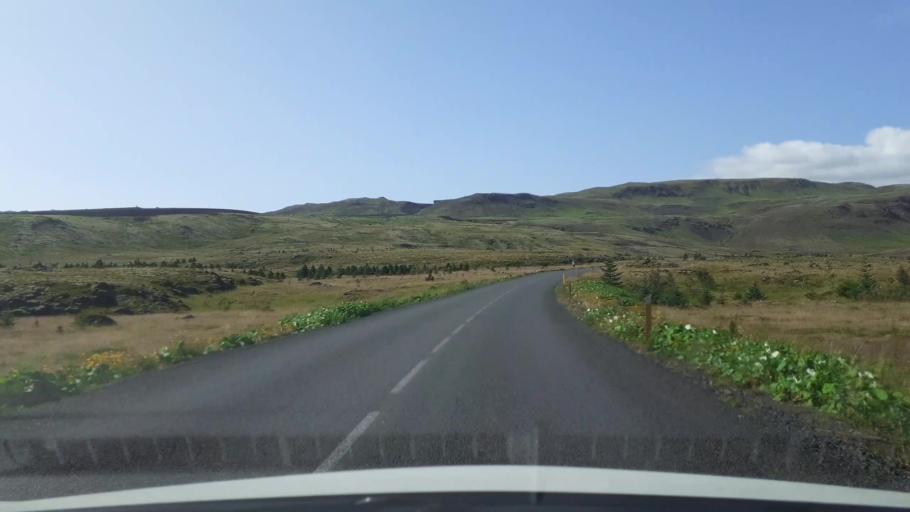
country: IS
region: South
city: Hveragerdi
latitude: 64.0132
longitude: -21.2043
